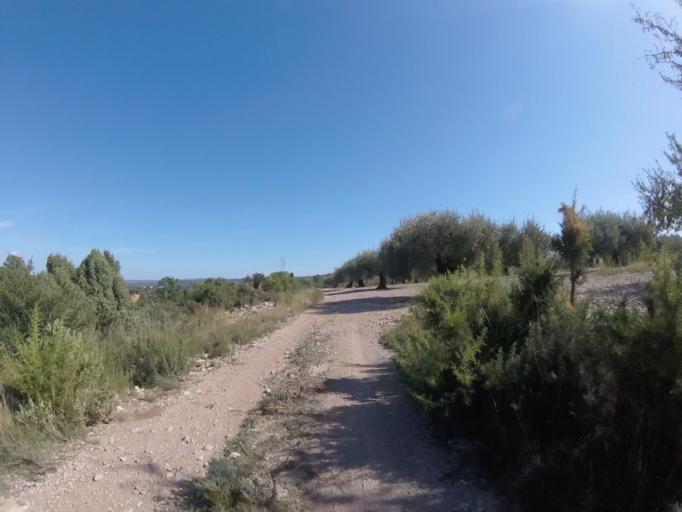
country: ES
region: Valencia
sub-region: Provincia de Castello
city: Sarratella
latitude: 40.2807
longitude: 0.0698
